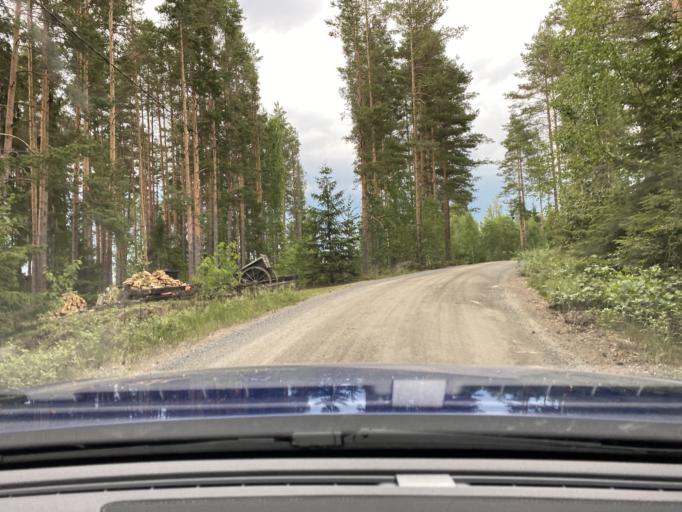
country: FI
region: Satakunta
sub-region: Rauma
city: Lappi
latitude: 61.1350
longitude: 21.9014
